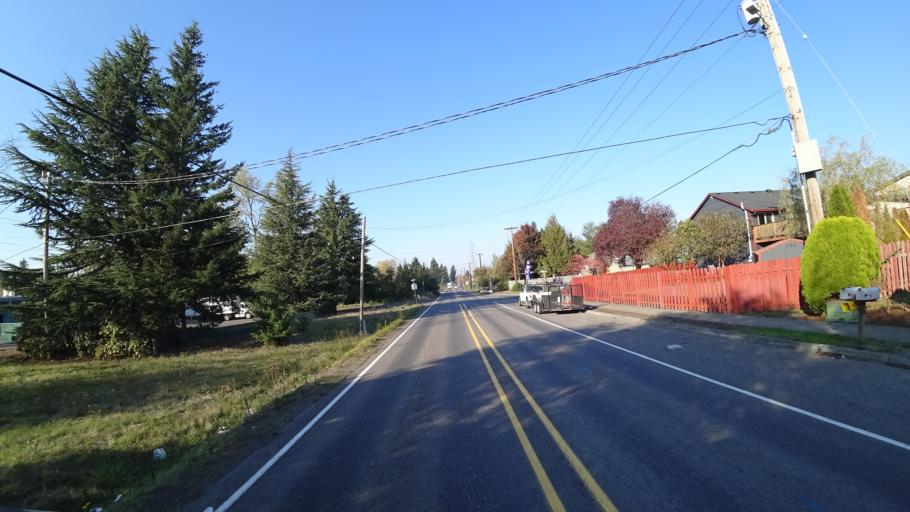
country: US
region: Oregon
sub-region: Multnomah County
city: Gresham
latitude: 45.5082
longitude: -122.4551
